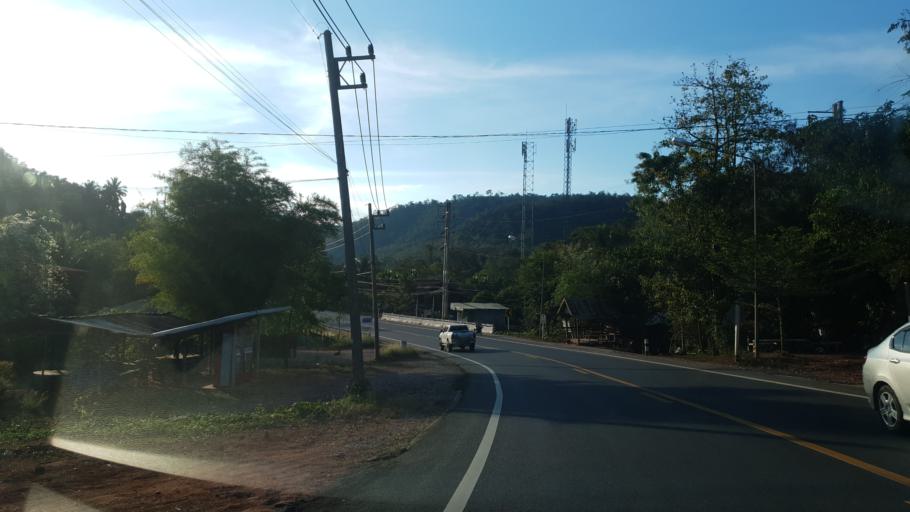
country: TH
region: Loei
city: Dan Sai
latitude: 17.2322
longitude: 101.0544
